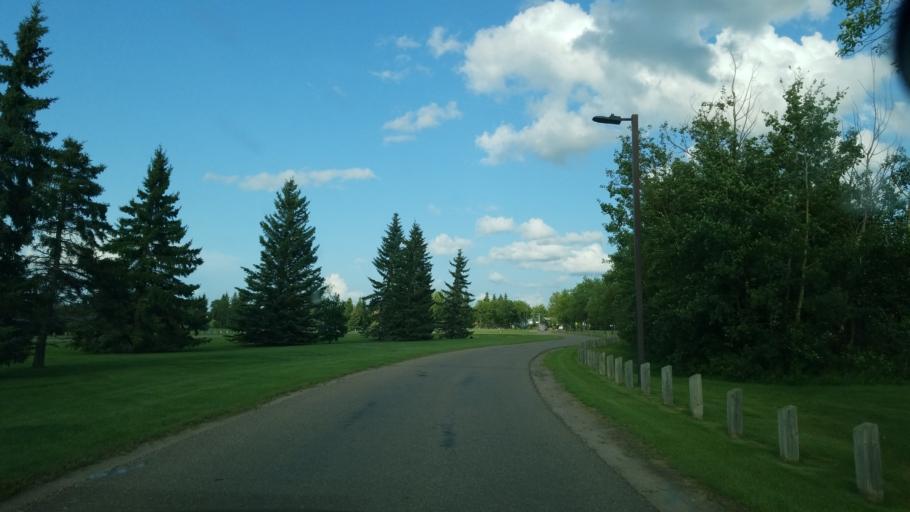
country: CA
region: Saskatchewan
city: Lloydminster
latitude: 53.2635
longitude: -110.0340
